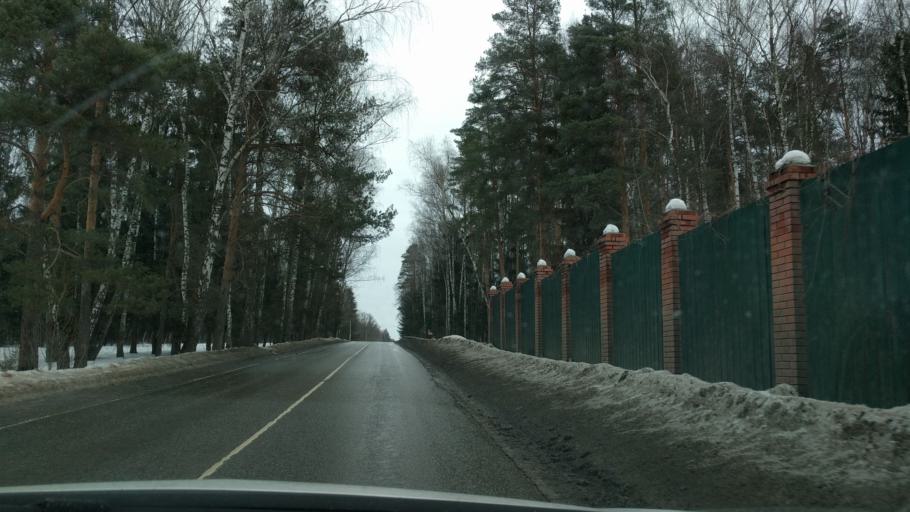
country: RU
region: Moskovskaya
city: Dubrovitsy
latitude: 55.4223
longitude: 37.4169
